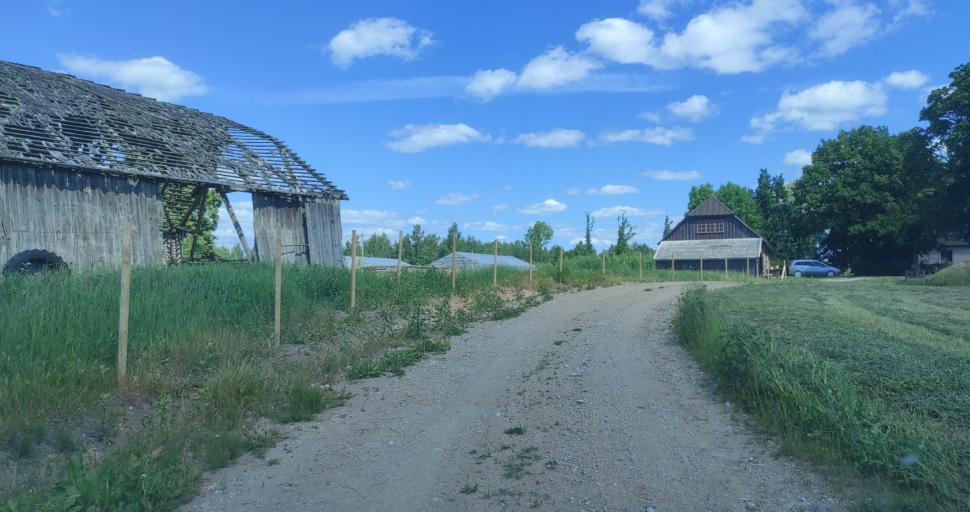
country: LV
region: Aizpute
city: Aizpute
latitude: 56.8689
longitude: 21.7190
